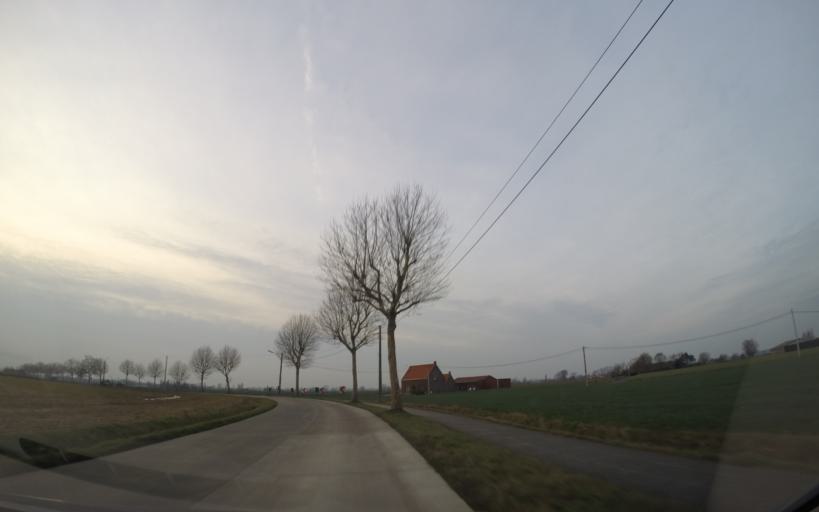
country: BE
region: Flanders
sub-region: Provincie West-Vlaanderen
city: Dentergem
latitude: 51.0098
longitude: 3.4661
